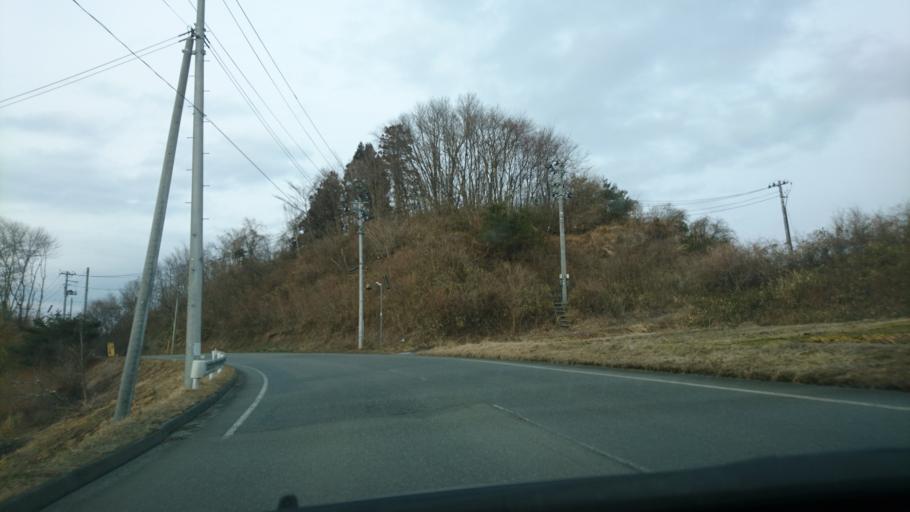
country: JP
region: Iwate
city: Ichinoseki
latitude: 38.9386
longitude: 141.3609
